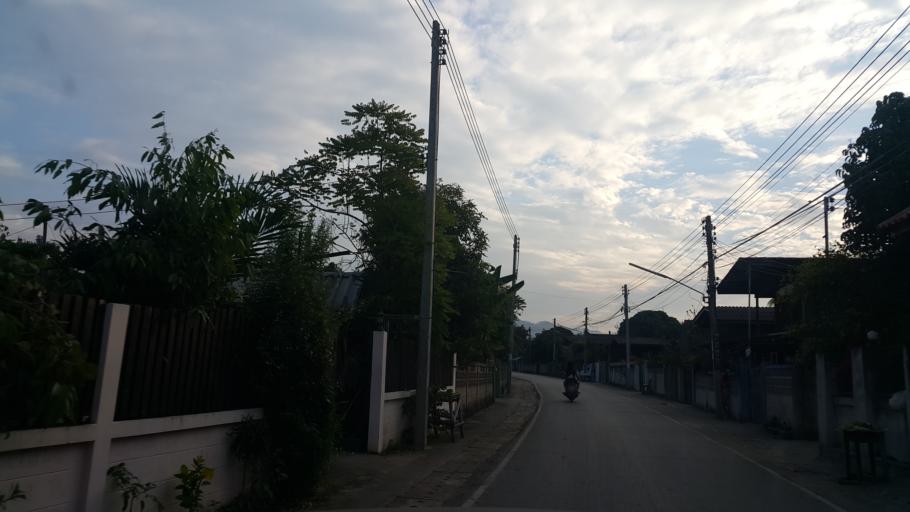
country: TH
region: Lampang
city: Sop Prap
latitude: 17.8680
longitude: 99.3309
